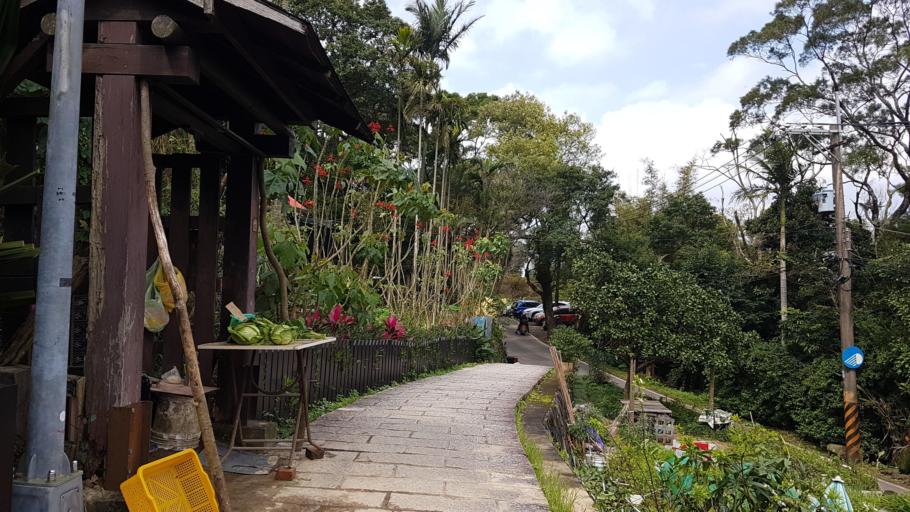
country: TW
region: Taipei
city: Taipei
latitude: 24.9704
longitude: 121.5806
